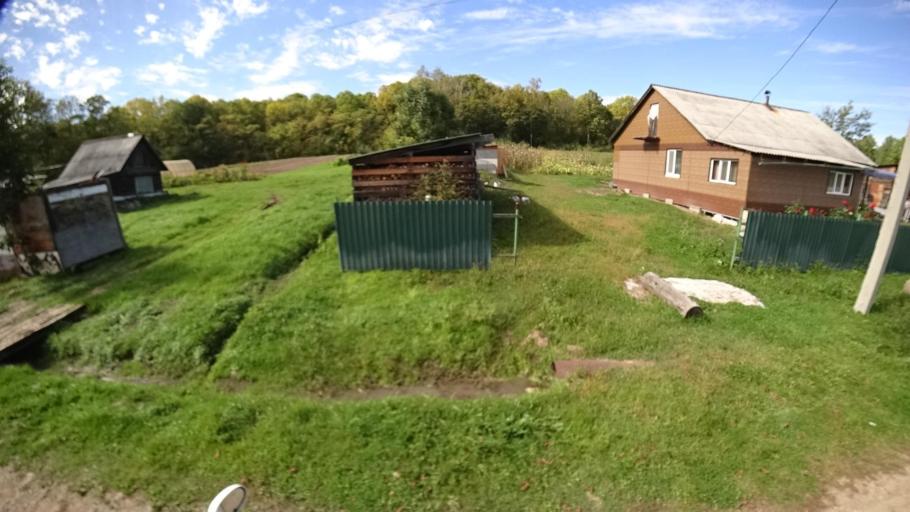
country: RU
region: Primorskiy
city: Yakovlevka
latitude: 44.3938
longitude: 133.5958
